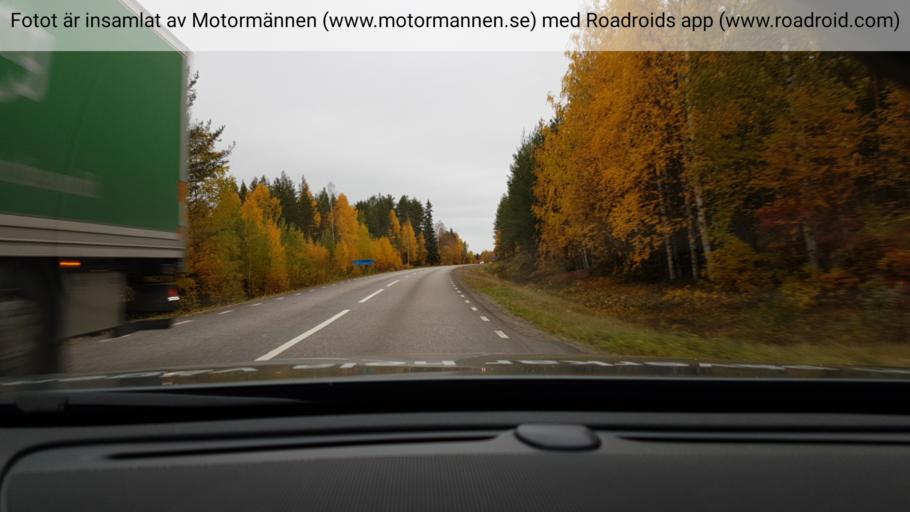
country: SE
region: Norrbotten
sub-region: Overkalix Kommun
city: OEverkalix
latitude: 66.4897
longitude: 22.7778
